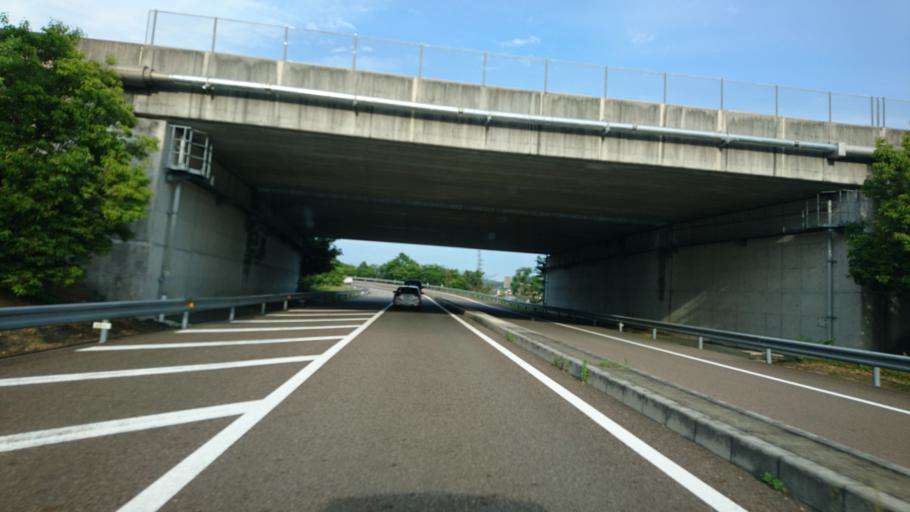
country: JP
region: Gifu
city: Mitake
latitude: 35.4318
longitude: 137.1001
